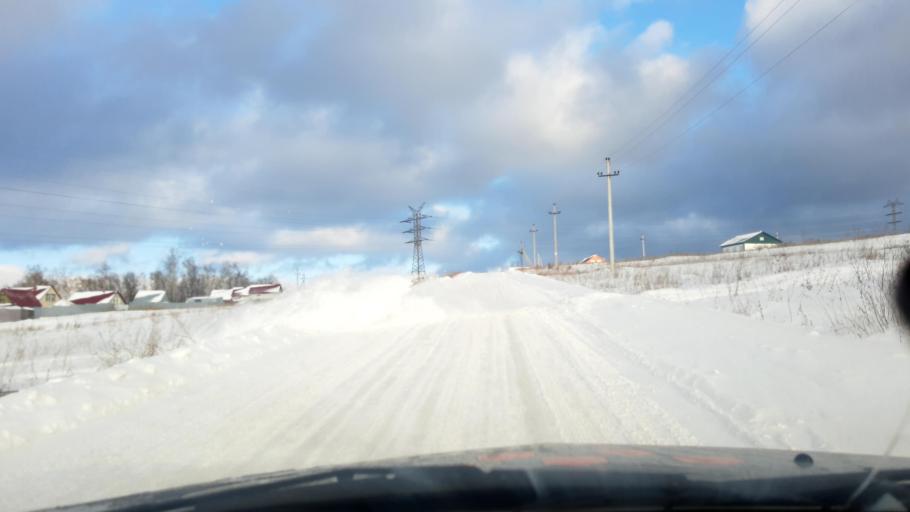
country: RU
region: Bashkortostan
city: Avdon
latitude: 54.6295
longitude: 55.6085
